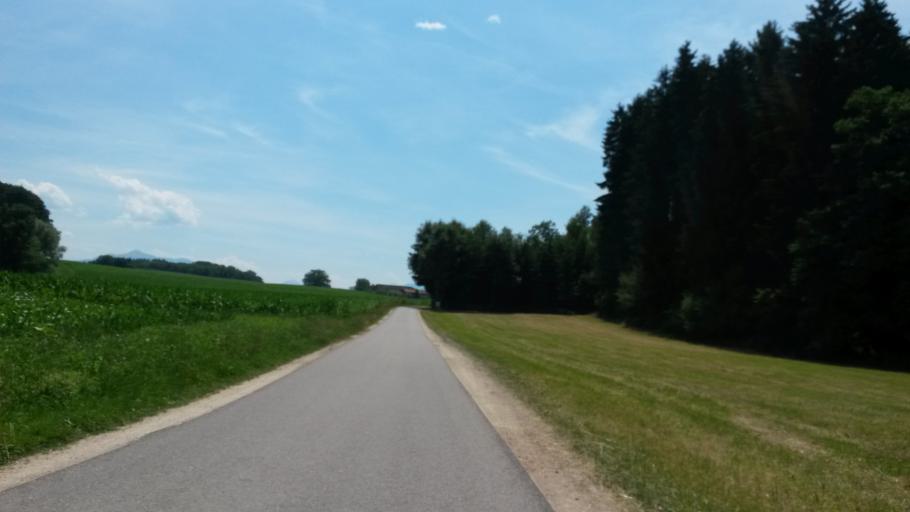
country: DE
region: Bavaria
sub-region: Upper Bavaria
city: Seeon-Seebruck
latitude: 47.9478
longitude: 12.4955
